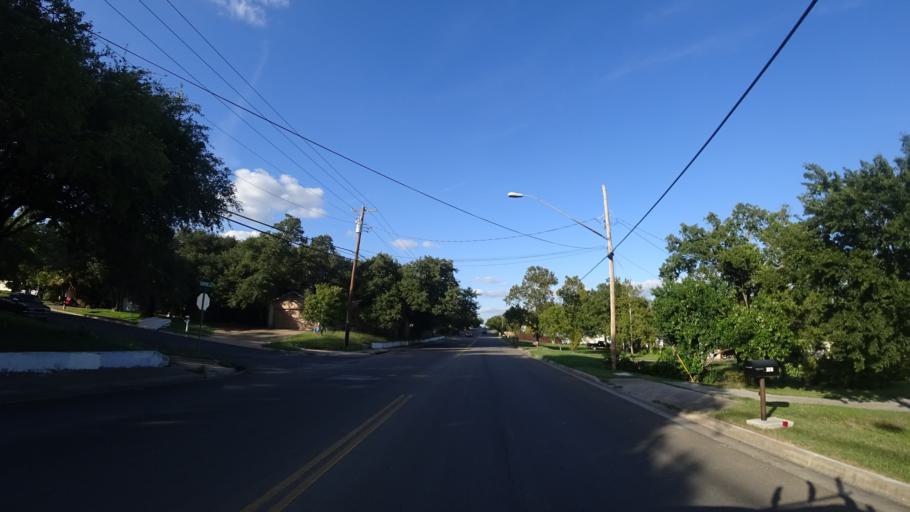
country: US
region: Texas
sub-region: Travis County
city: Onion Creek
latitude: 30.1940
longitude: -97.7940
